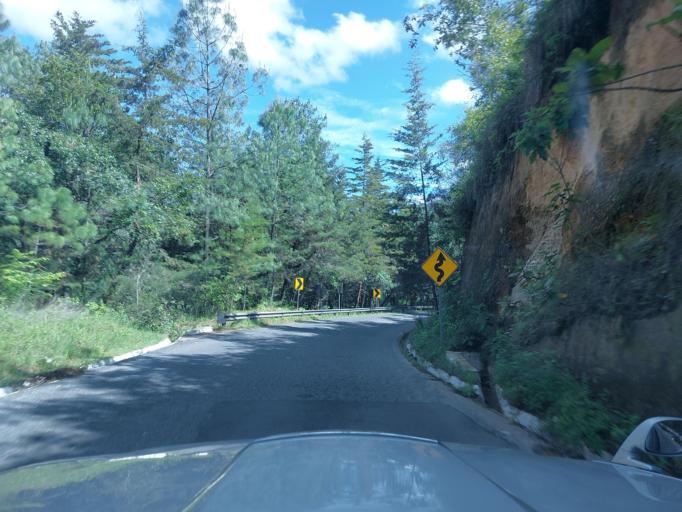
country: GT
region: Chimaltenango
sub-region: Municipio de Santa Cruz Balanya
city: Santa Cruz Balanya
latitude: 14.6904
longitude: -90.8974
